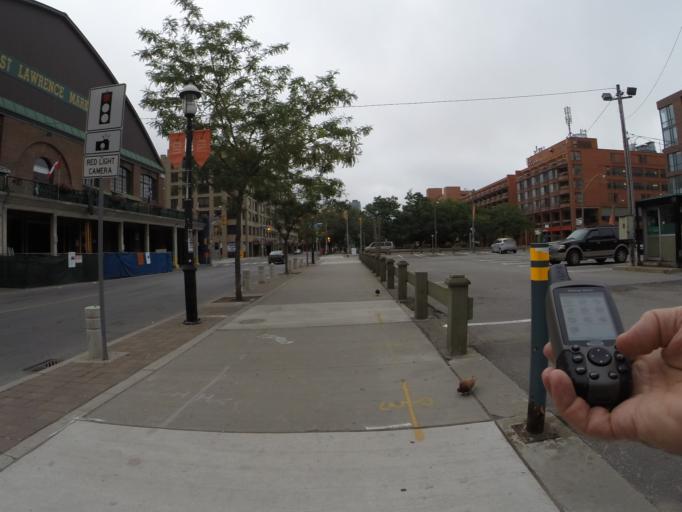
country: CA
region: Ontario
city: Toronto
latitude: 43.6524
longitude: -79.3756
